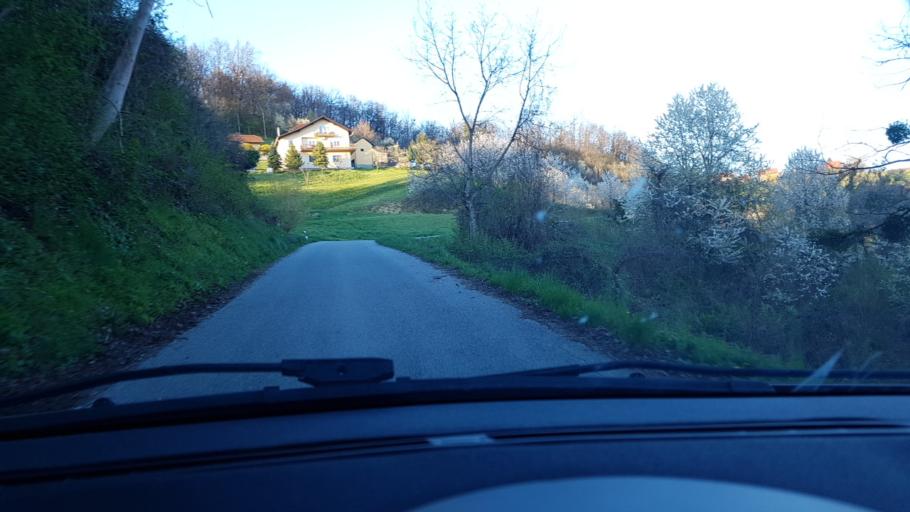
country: HR
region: Krapinsko-Zagorska
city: Pregrada
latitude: 46.1659
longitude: 15.7033
